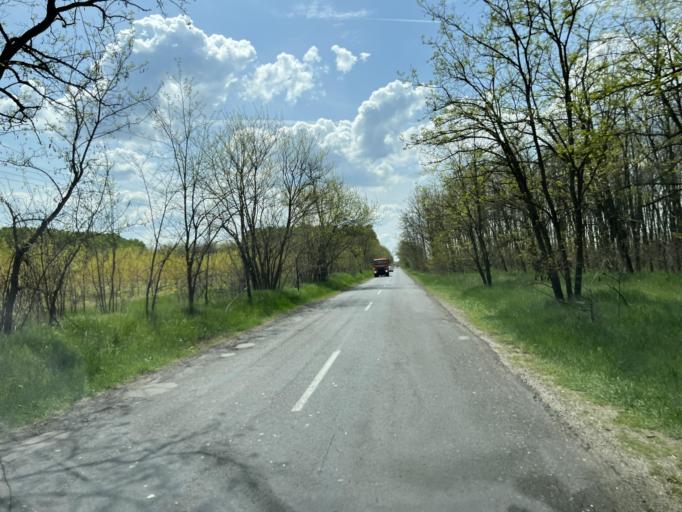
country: HU
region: Pest
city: Csemo
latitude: 47.1252
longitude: 19.7055
